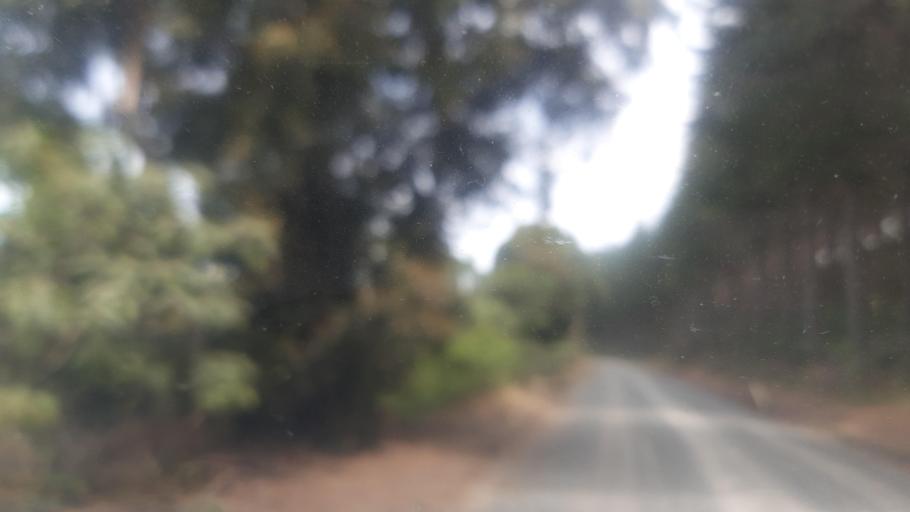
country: NZ
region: Northland
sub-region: Far North District
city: Kaitaia
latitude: -35.0167
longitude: 173.2051
